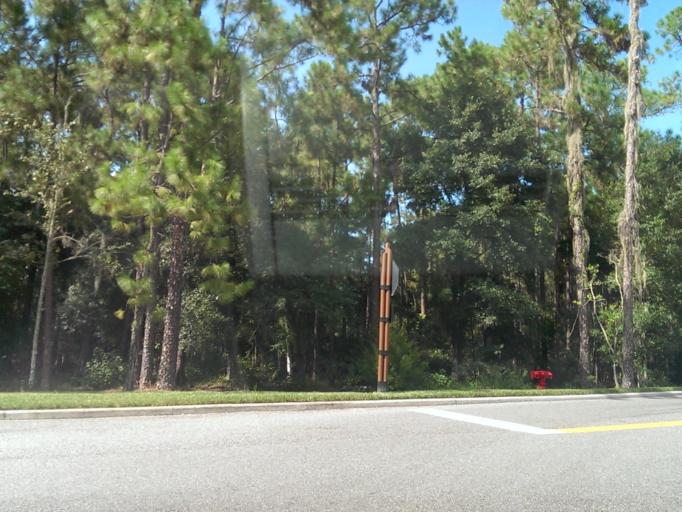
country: US
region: Florida
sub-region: Orange County
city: Bay Hill
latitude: 28.4065
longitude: -81.5736
